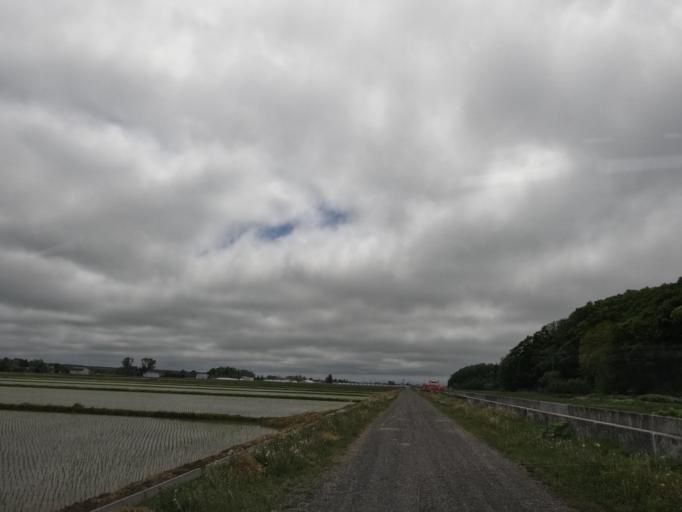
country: JP
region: Hokkaido
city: Tobetsu
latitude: 43.2688
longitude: 141.5236
